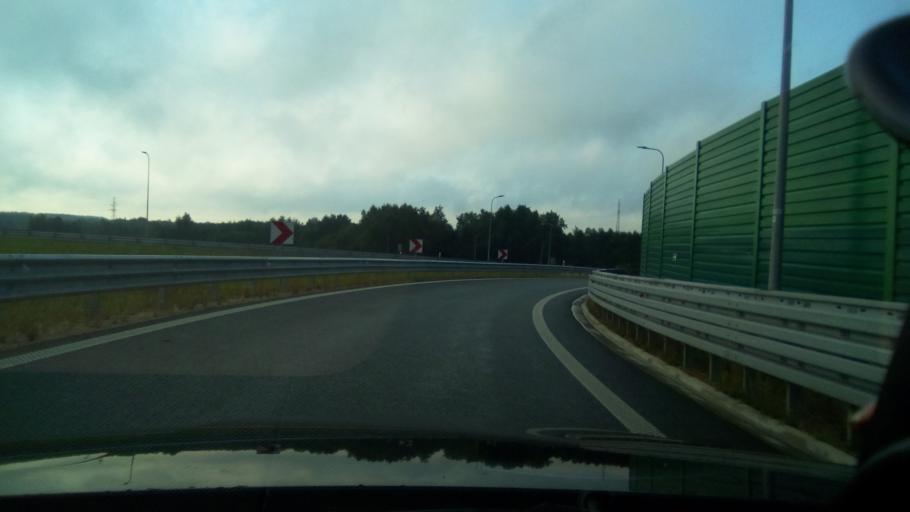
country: PL
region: Silesian Voivodeship
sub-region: Powiat czestochowski
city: Konopiska
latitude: 50.7449
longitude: 19.0434
